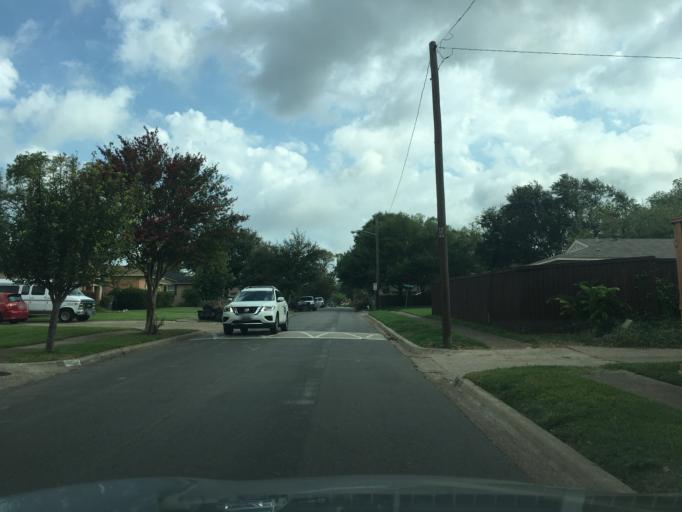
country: US
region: Texas
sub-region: Dallas County
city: Richardson
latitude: 32.8975
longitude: -96.7570
